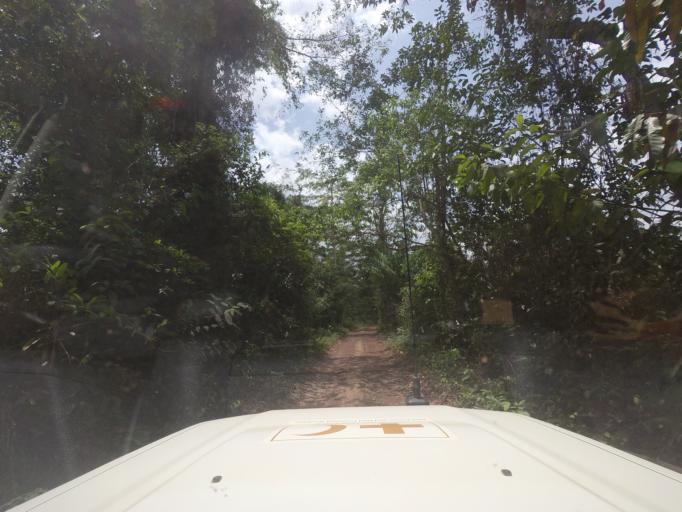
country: LR
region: Bong
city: Gbarnga
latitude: 7.1899
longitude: -9.1984
